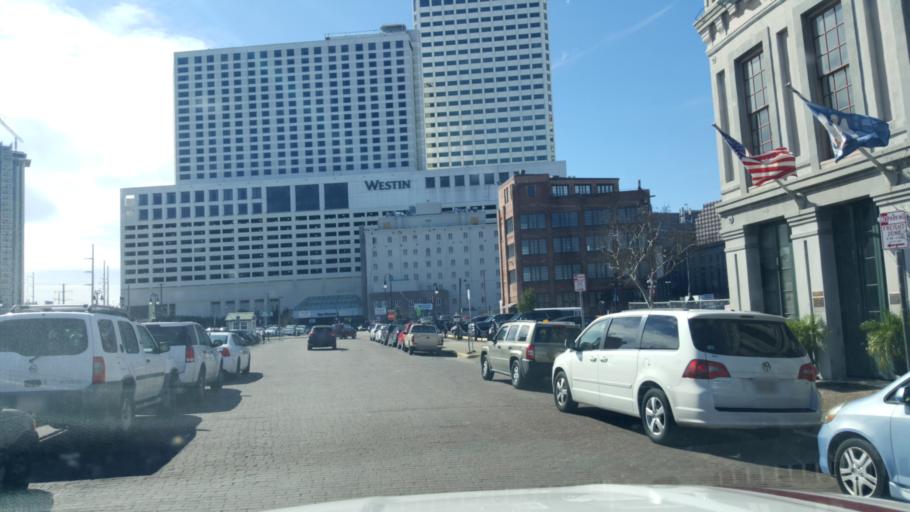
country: US
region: Louisiana
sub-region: Orleans Parish
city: New Orleans
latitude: 29.9534
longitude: -90.0638
